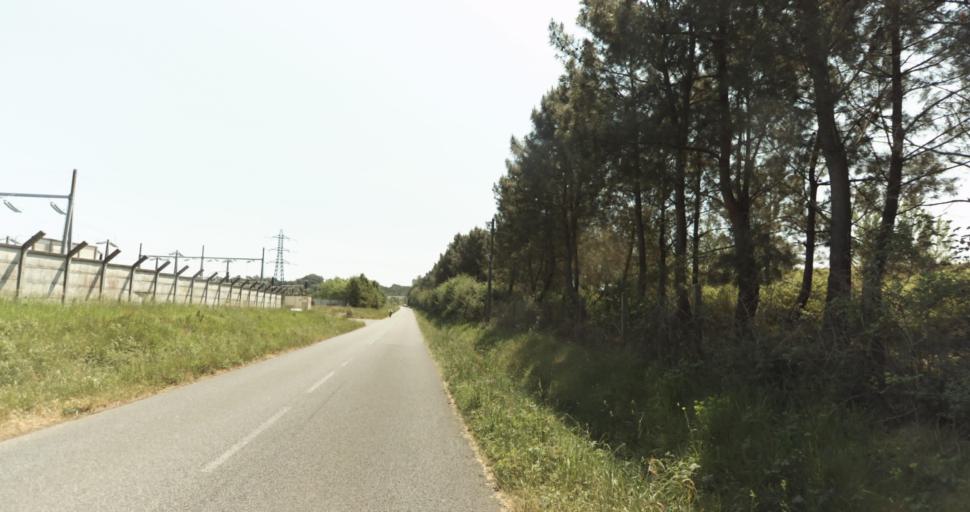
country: FR
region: Midi-Pyrenees
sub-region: Departement de la Haute-Garonne
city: La Salvetat-Saint-Gilles
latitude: 43.5978
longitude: 1.2731
